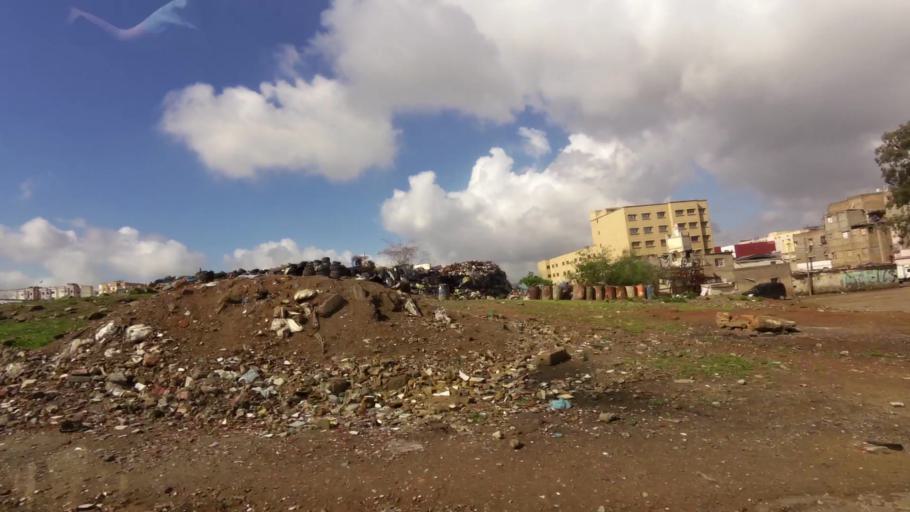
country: MA
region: Grand Casablanca
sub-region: Nouaceur
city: Bouskoura
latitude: 33.5278
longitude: -7.6759
